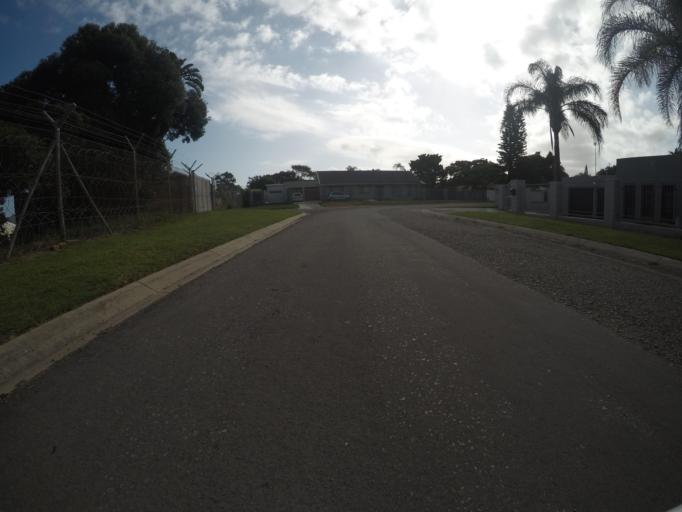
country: ZA
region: Eastern Cape
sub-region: Buffalo City Metropolitan Municipality
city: East London
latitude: -32.9698
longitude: 27.9521
